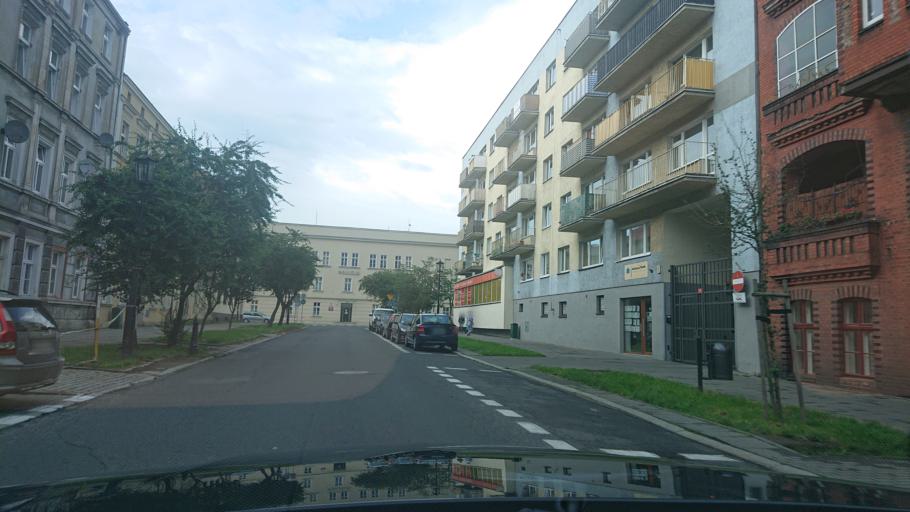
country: PL
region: Greater Poland Voivodeship
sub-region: Powiat gnieznienski
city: Gniezno
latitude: 52.5351
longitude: 17.6038
